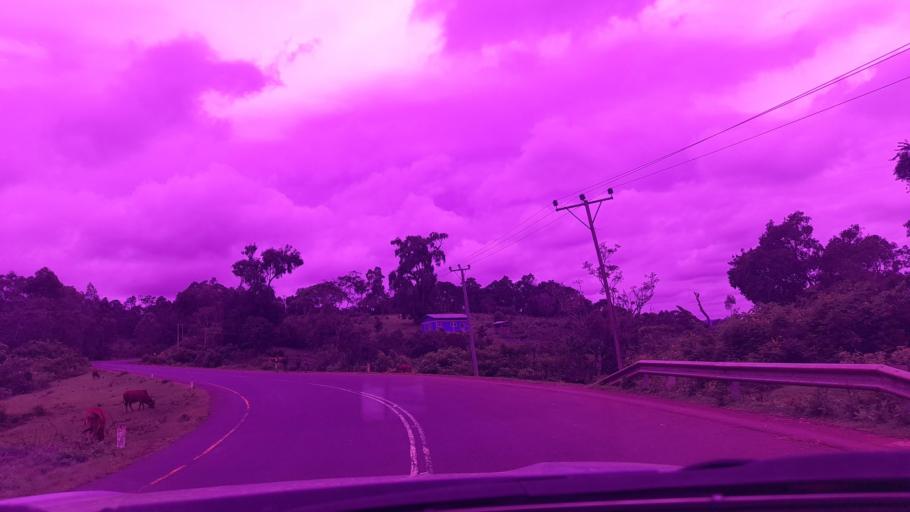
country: ET
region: Southern Nations, Nationalities, and People's Region
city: Bonga
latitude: 7.2923
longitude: 35.9795
